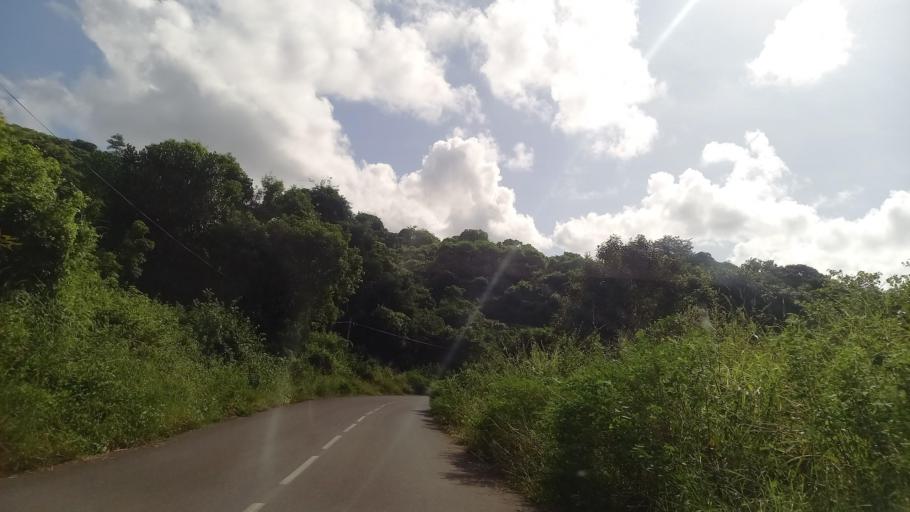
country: YT
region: Kani-Keli
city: Kani Keli
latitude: -12.9860
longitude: 45.1345
